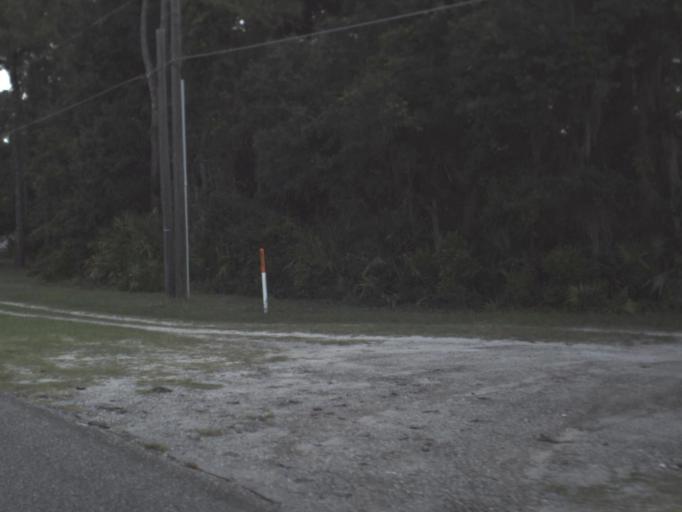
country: US
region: Florida
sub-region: Putnam County
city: Crescent City
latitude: 29.4607
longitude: -81.5218
